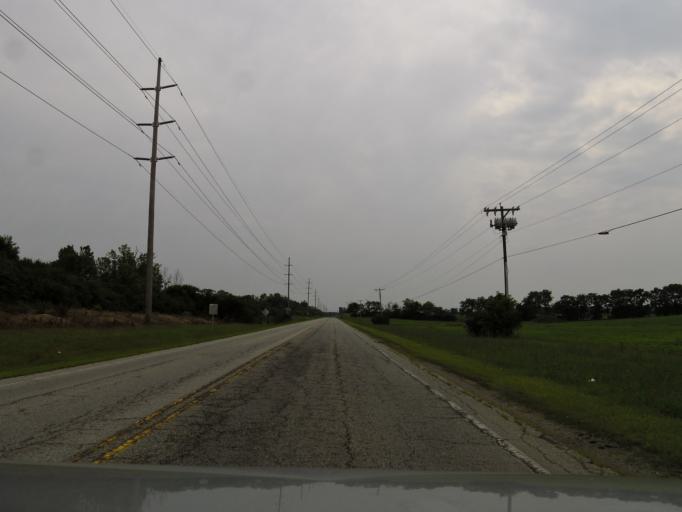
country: US
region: Ohio
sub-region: Clinton County
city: Wilmington
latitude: 39.4113
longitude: -83.8465
